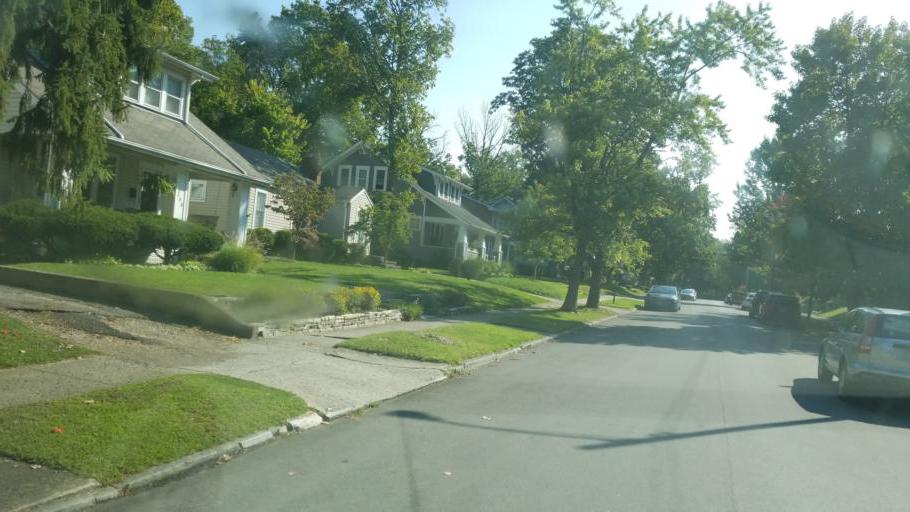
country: US
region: Ohio
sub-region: Franklin County
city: Grandview Heights
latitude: 40.0301
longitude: -83.0097
